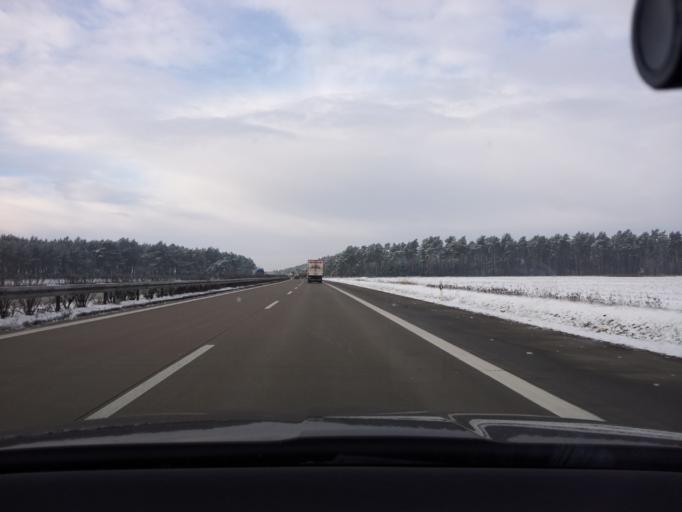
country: DE
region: Mecklenburg-Vorpommern
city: Rastow
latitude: 53.4320
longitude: 11.4686
